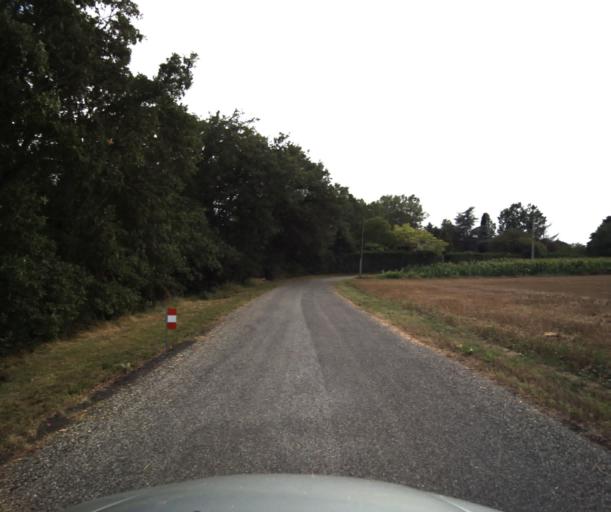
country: FR
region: Midi-Pyrenees
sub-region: Departement de la Haute-Garonne
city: Le Fauga
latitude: 43.4253
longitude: 1.3148
